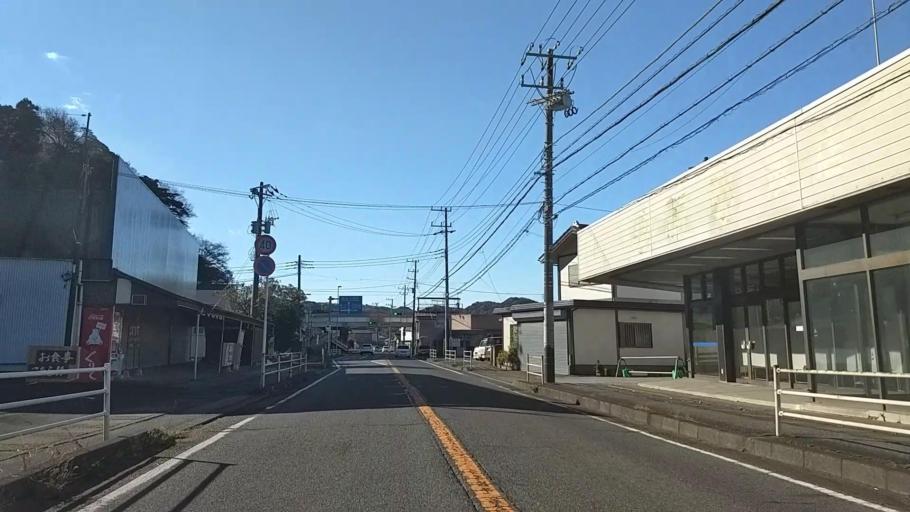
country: JP
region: Chiba
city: Futtsu
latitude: 35.2225
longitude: 139.8734
